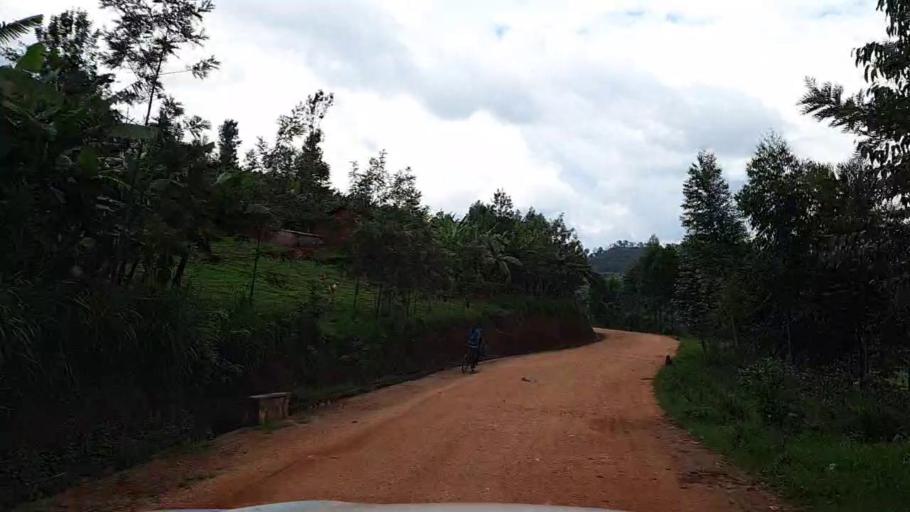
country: RW
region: Southern Province
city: Nyanza
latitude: -2.4114
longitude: 29.6736
